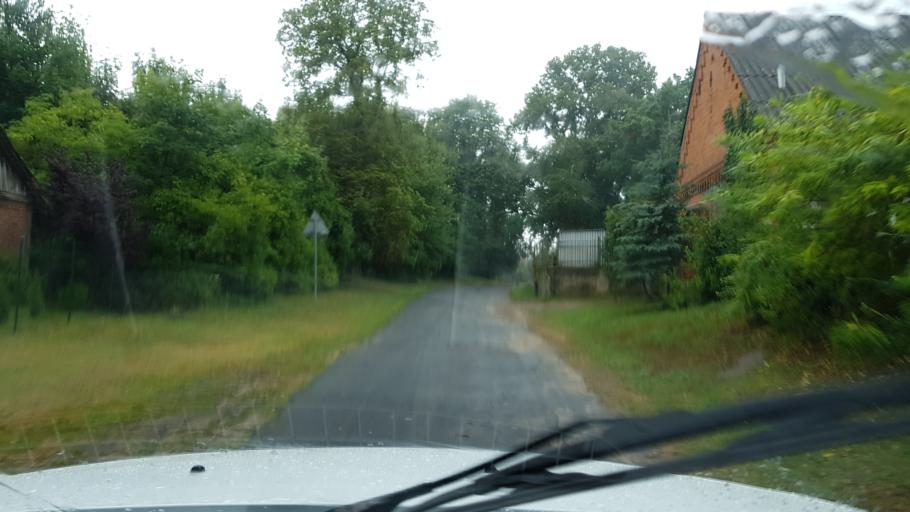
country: PL
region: West Pomeranian Voivodeship
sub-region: Powiat mysliborski
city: Barlinek
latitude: 52.9903
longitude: 15.1230
